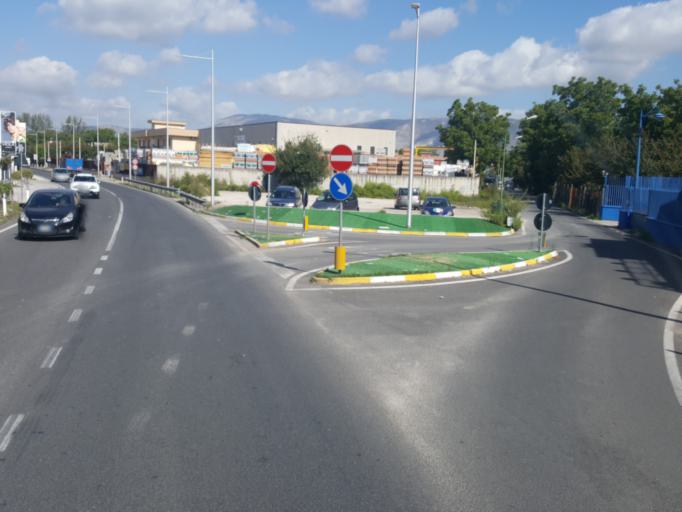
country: IT
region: Campania
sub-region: Provincia di Napoli
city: Nola
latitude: 40.9205
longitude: 14.5143
